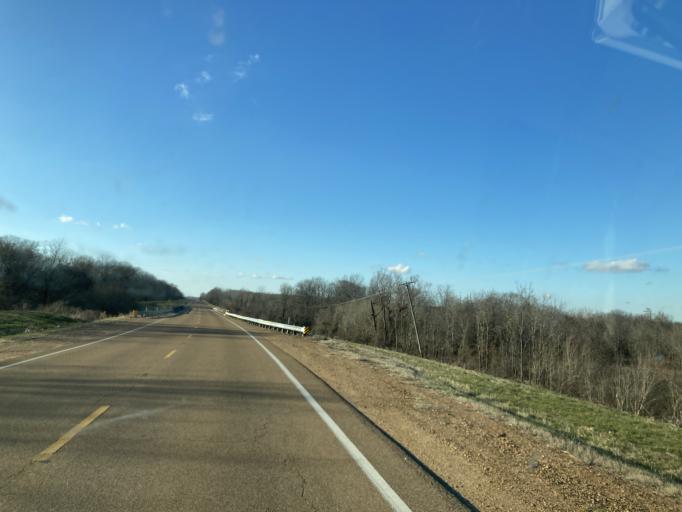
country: US
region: Mississippi
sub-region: Yazoo County
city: Yazoo City
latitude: 32.9182
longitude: -90.5566
